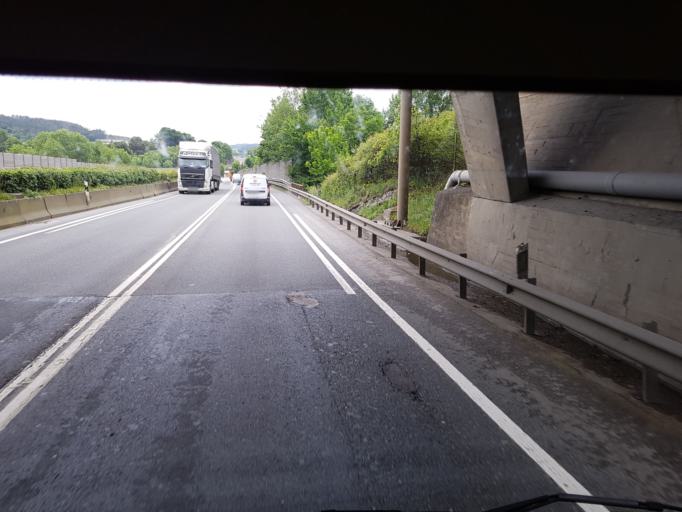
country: ES
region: Basque Country
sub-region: Bizkaia
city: Amorebieta
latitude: 43.2243
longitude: -2.7316
